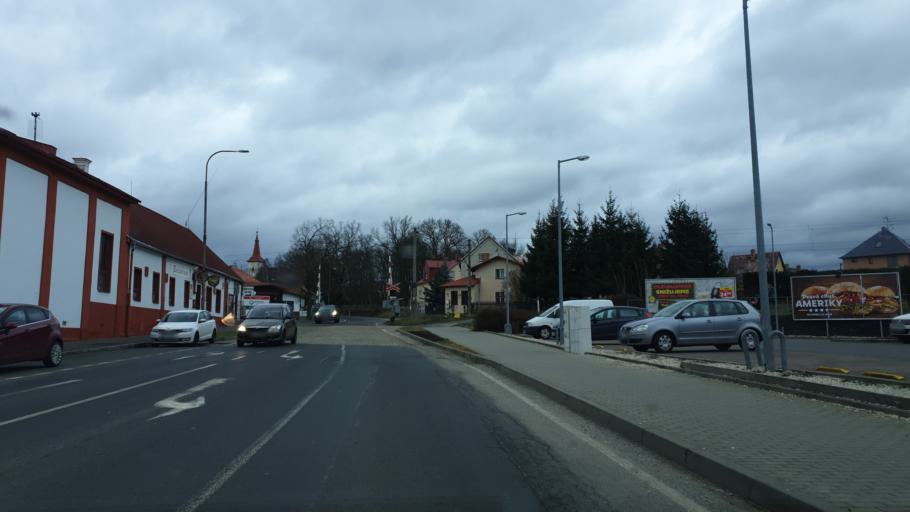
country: CZ
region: Karlovarsky
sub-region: Okres Cheb
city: Frantiskovy Lazne
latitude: 50.1274
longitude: 12.3460
